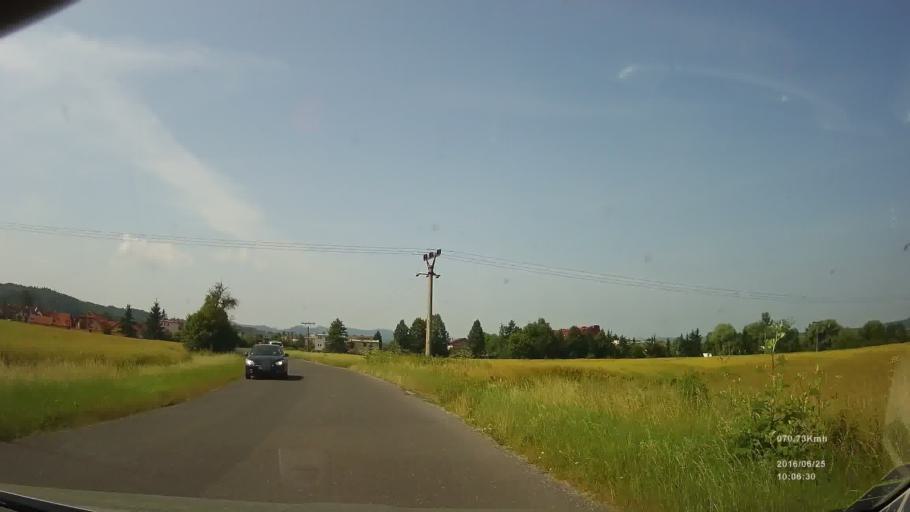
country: SK
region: Banskobystricky
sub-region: Okres Banska Bystrica
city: Zvolen
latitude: 48.6198
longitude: 19.1484
